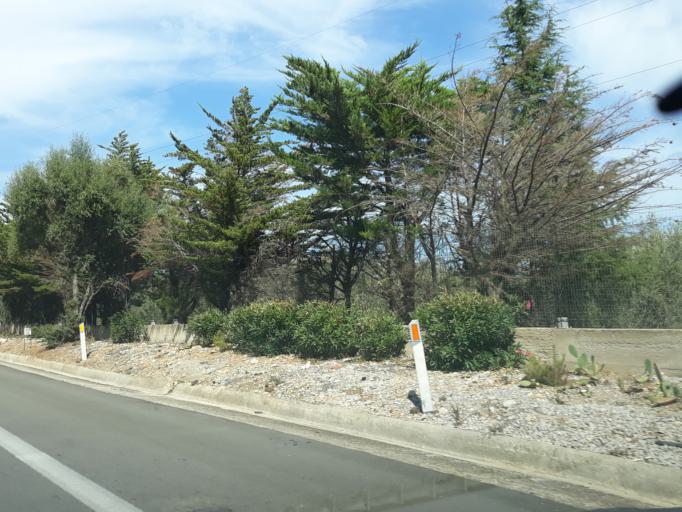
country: IT
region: Sicily
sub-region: Palermo
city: Trabia
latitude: 37.9842
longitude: 13.6592
